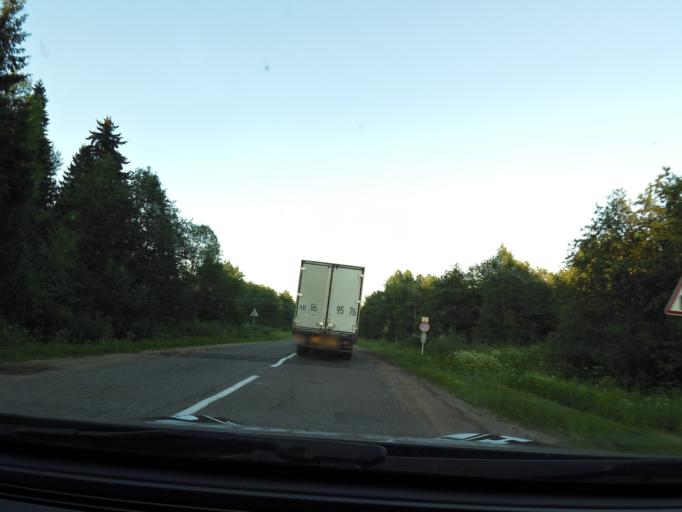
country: RU
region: Jaroslavl
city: Prechistoye
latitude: 58.4096
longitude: 40.3644
